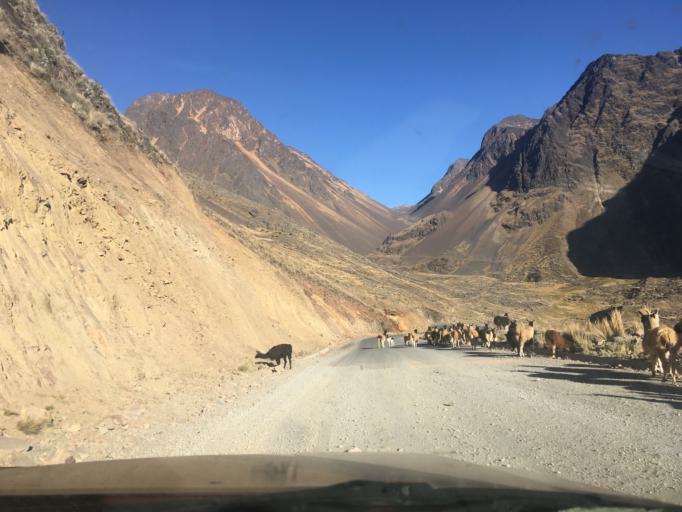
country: BO
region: La Paz
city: Quime
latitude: -17.0280
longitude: -67.2882
